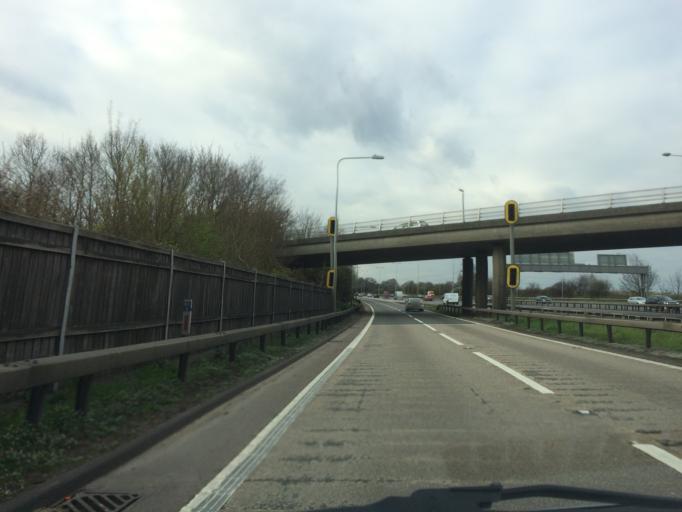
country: GB
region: England
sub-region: Surrey
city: Chertsey
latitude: 51.3769
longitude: -0.5108
